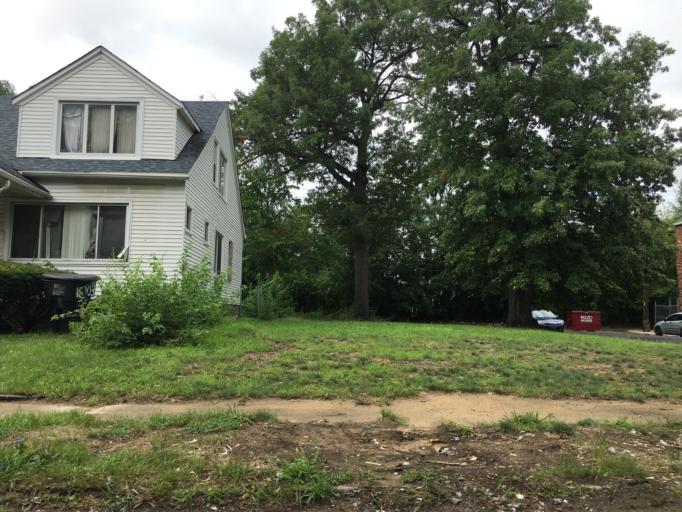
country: US
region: Michigan
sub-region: Wayne County
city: Highland Park
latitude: 42.4073
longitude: -83.1497
